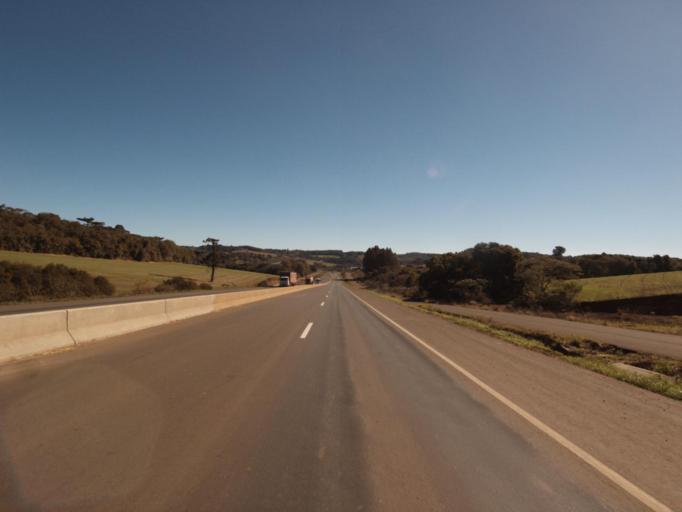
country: BR
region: Santa Catarina
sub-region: Xanxere
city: Xanxere
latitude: -26.8860
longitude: -52.4259
